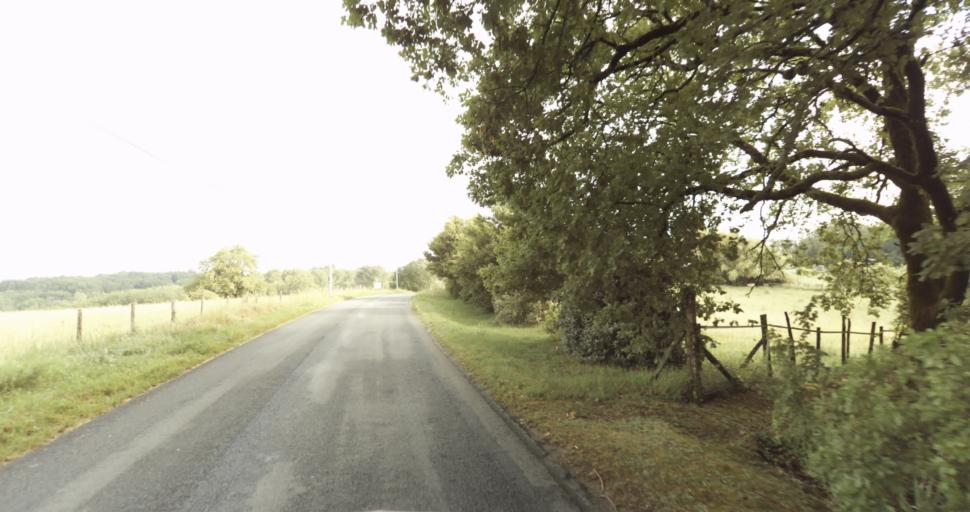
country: FR
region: Aquitaine
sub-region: Departement de la Dordogne
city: Le Bugue
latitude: 44.9242
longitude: 0.8224
